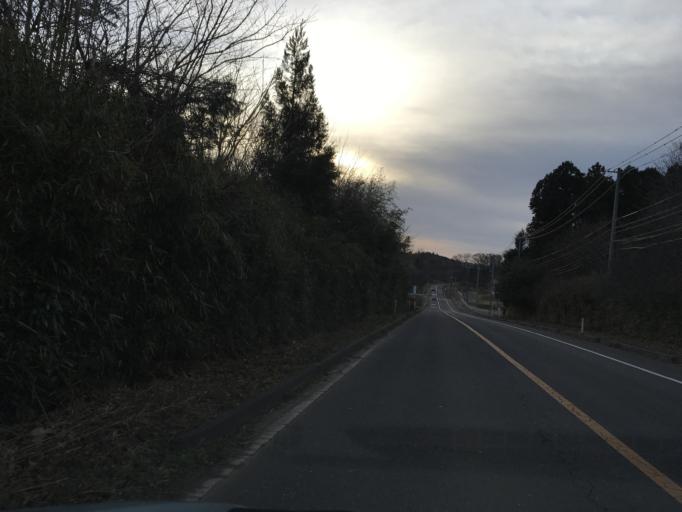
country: JP
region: Miyagi
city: Kogota
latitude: 38.6705
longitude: 141.0854
